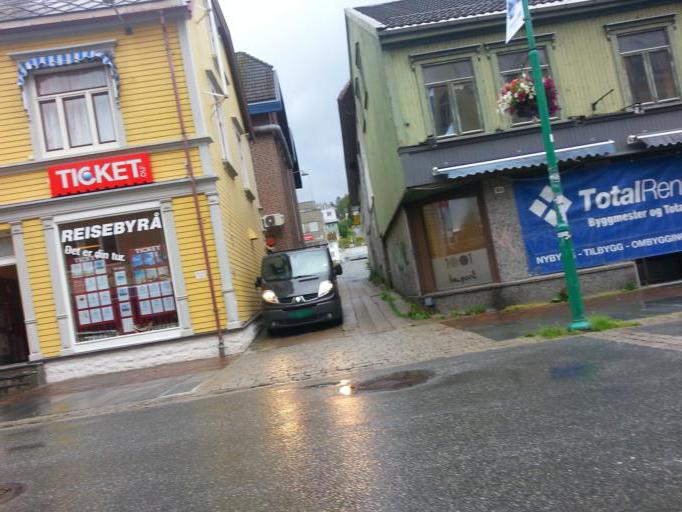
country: NO
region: Troms
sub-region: Tromso
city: Tromso
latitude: 69.6520
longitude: 18.9586
